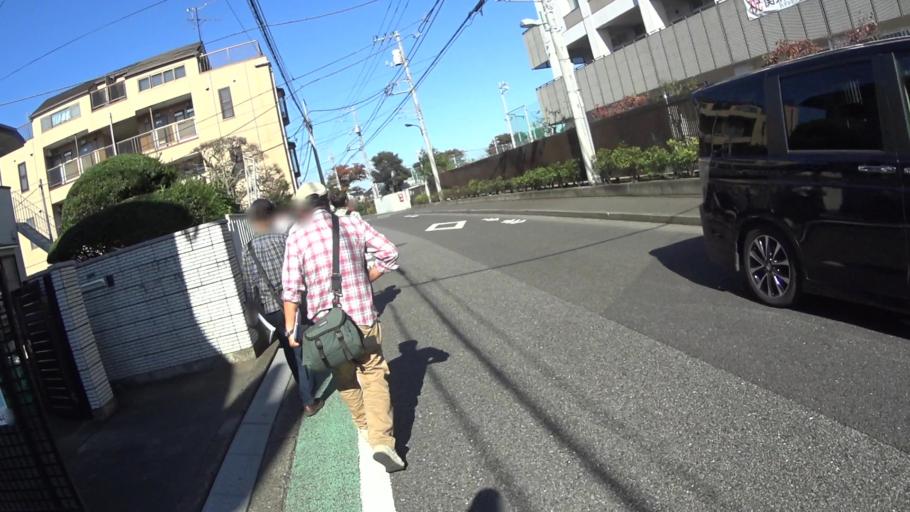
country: JP
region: Tokyo
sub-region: Machida-shi
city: Machida
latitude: 35.5546
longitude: 139.4486
